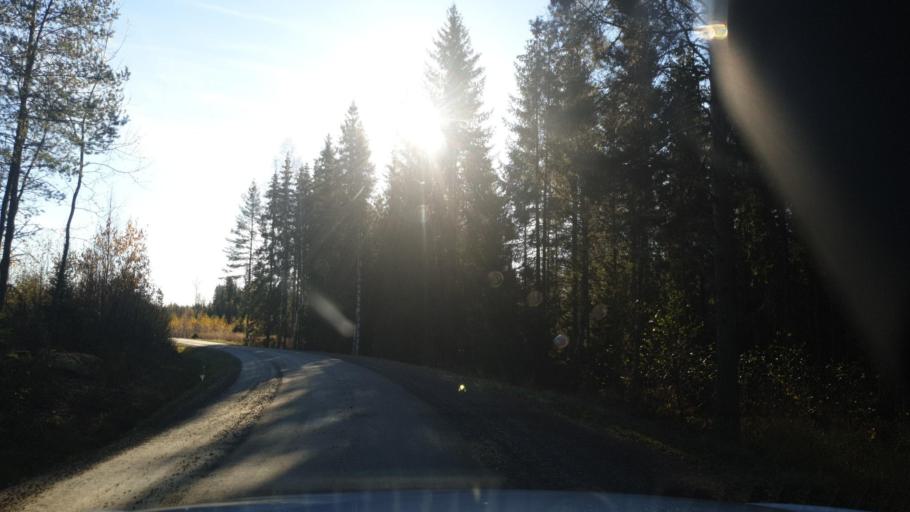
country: SE
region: Vaermland
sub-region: Karlstads Kommun
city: Edsvalla
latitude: 59.4841
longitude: 13.0687
